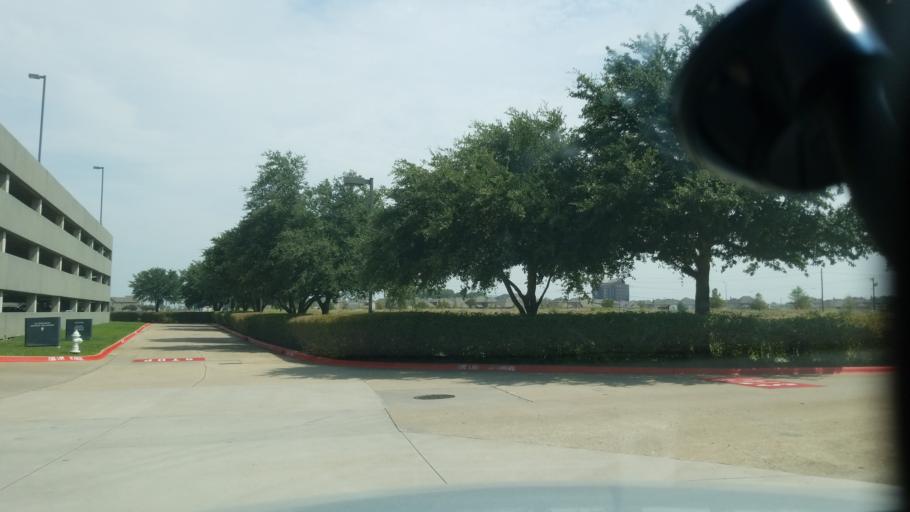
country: US
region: Texas
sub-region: Dallas County
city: Farmers Branch
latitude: 32.9097
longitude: -96.9252
